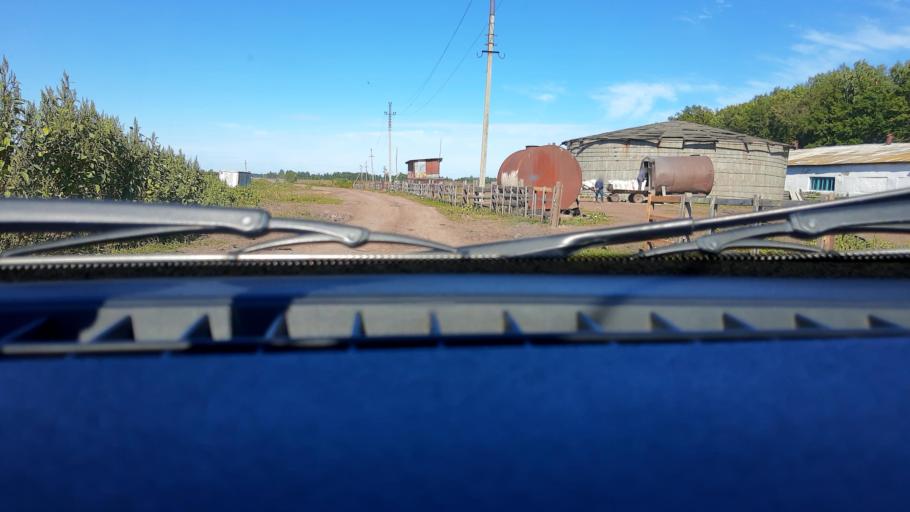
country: RU
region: Bashkortostan
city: Asanovo
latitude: 54.8189
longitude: 55.6228
